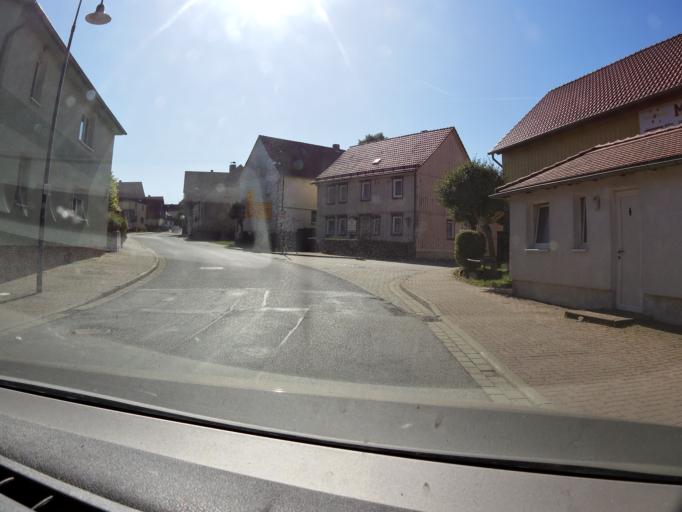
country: DE
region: Saxony-Anhalt
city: Friedrichsbrunn
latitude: 51.6789
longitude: 10.9683
